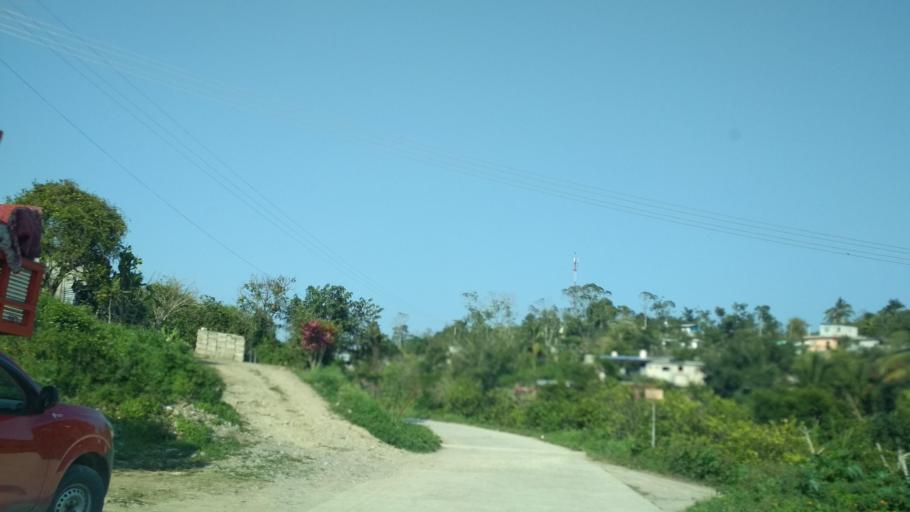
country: MX
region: Veracruz
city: Agua Dulce
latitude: 20.3894
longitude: -97.2116
